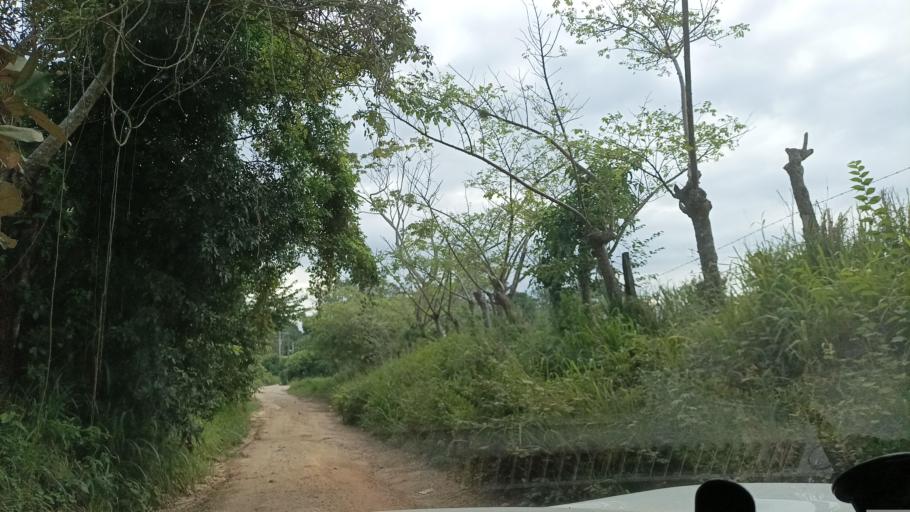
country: MX
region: Veracruz
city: Oluta
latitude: 17.9271
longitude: -94.8842
